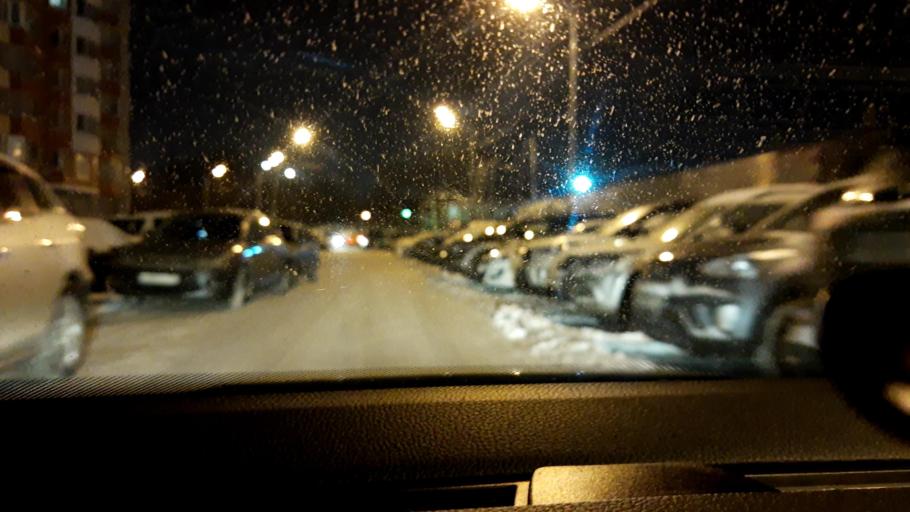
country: RU
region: Moscow
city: Khimki
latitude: 55.8763
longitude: 37.3878
